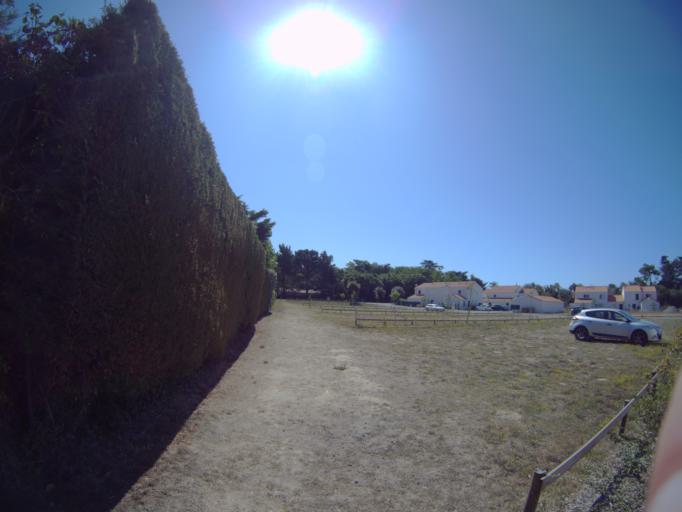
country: FR
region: Pays de la Loire
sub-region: Departement de la Vendee
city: Jard-sur-Mer
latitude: 46.4094
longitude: -1.5480
